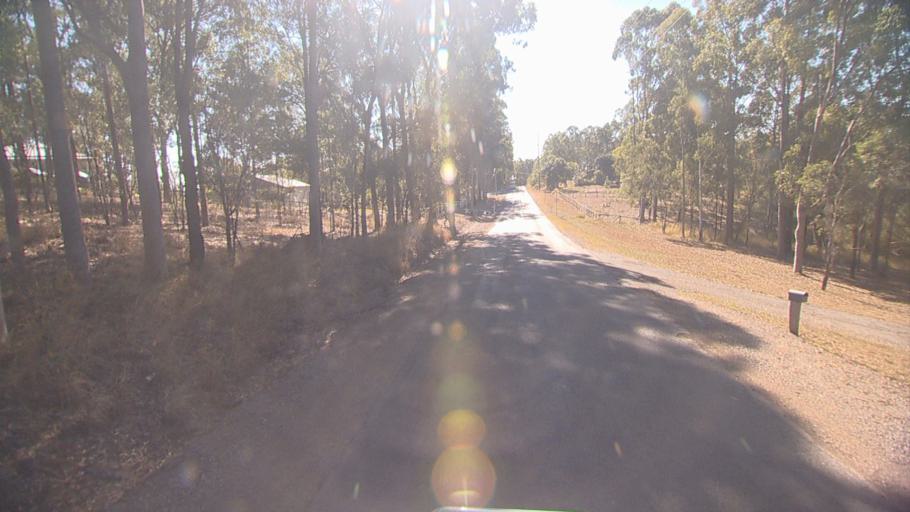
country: AU
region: Queensland
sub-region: Logan
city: Cedar Vale
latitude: -27.8883
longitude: 153.0167
